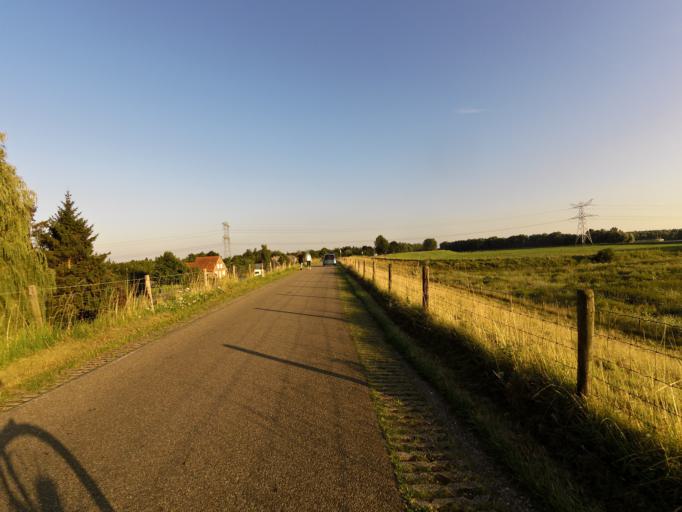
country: NL
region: Gelderland
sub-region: Gemeente Duiven
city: Duiven
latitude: 51.9242
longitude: 5.9910
